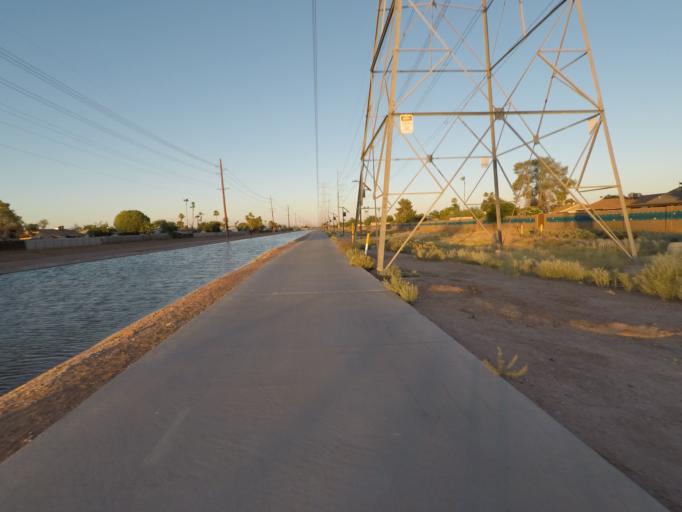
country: US
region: Arizona
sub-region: Maricopa County
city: San Carlos
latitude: 33.3567
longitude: -111.8852
